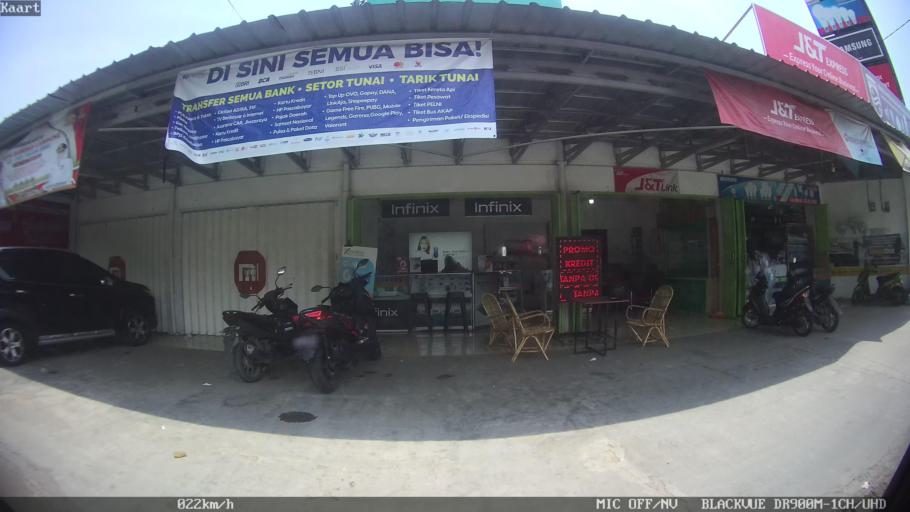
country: ID
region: Lampung
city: Bandarlampung
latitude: -5.4450
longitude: 105.2554
